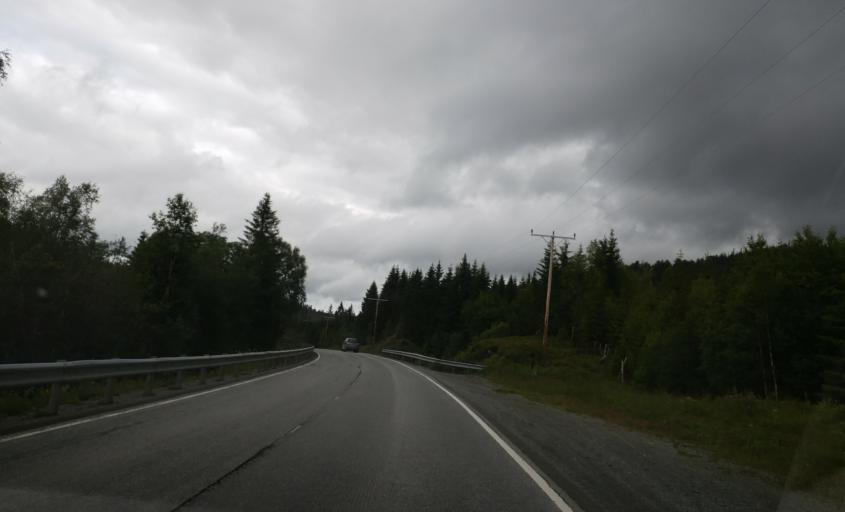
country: NO
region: Sor-Trondelag
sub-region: Selbu
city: Mebonden
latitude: 63.3484
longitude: 11.0787
